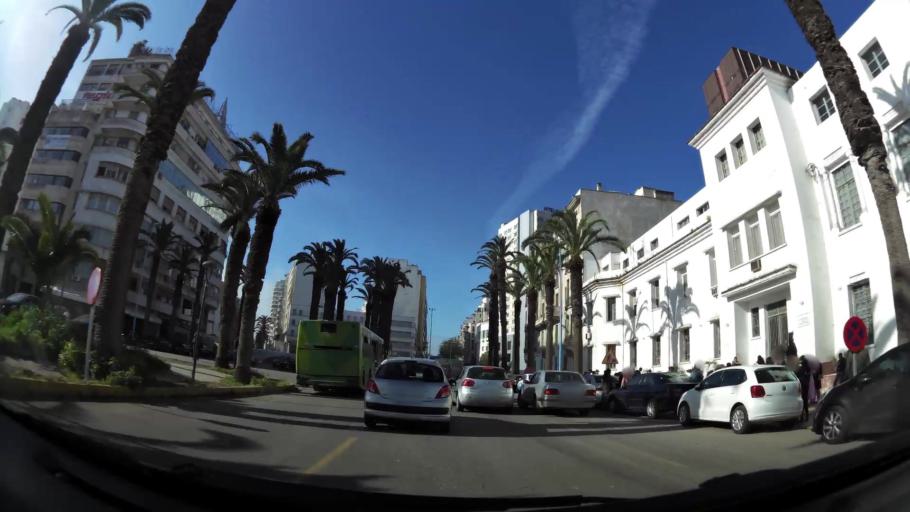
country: MA
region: Grand Casablanca
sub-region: Casablanca
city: Casablanca
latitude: 33.5977
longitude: -7.6091
